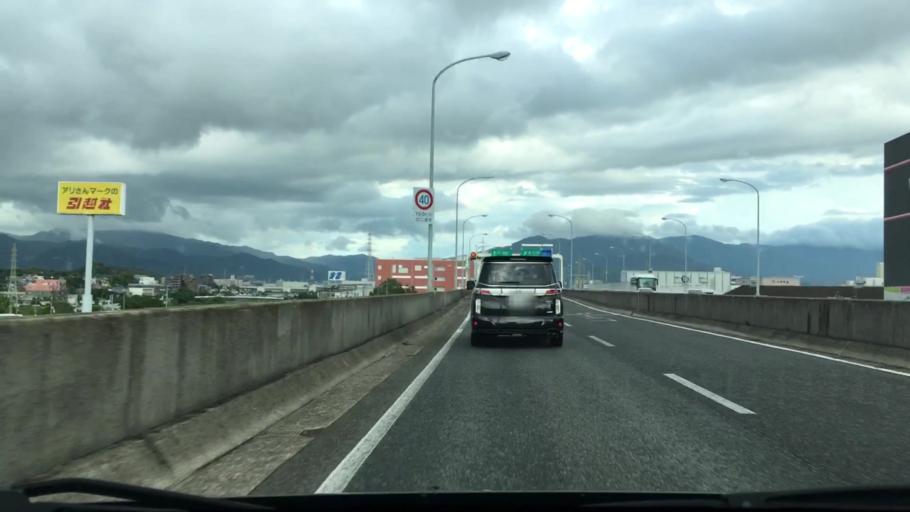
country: JP
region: Fukuoka
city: Fukuoka-shi
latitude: 33.6294
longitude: 130.4445
